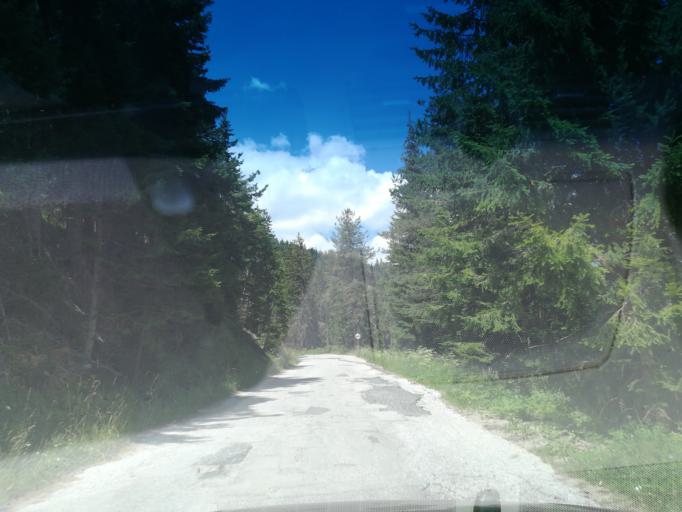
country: BG
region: Smolyan
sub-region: Obshtina Chepelare
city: Chepelare
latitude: 41.6810
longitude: 24.7711
